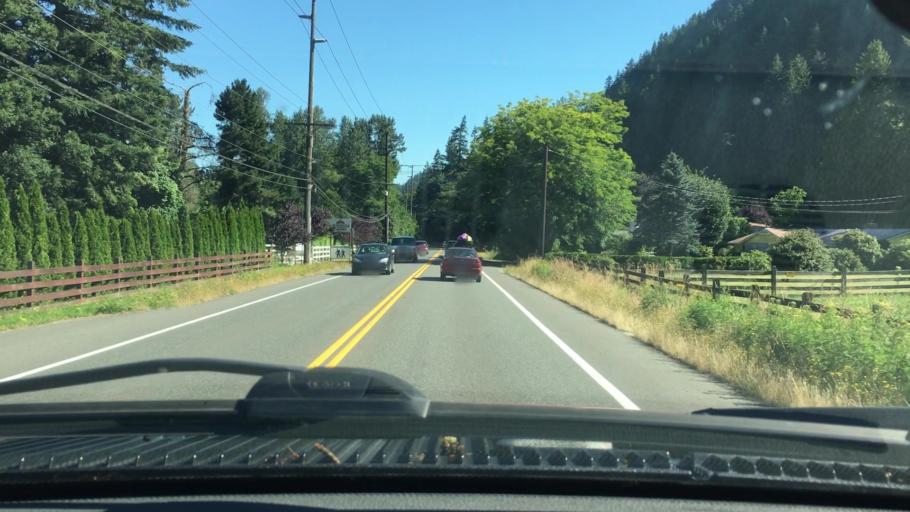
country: US
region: Washington
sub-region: King County
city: Issaquah
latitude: 47.4921
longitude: -122.0234
